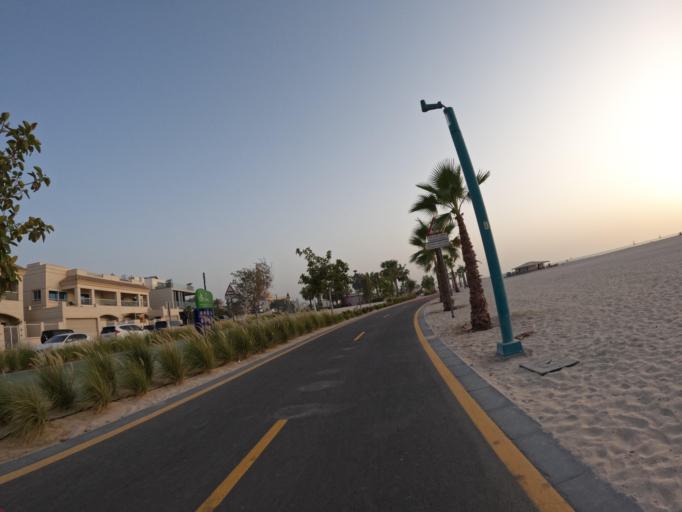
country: AE
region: Dubai
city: Dubai
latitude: 25.1702
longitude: 55.2136
